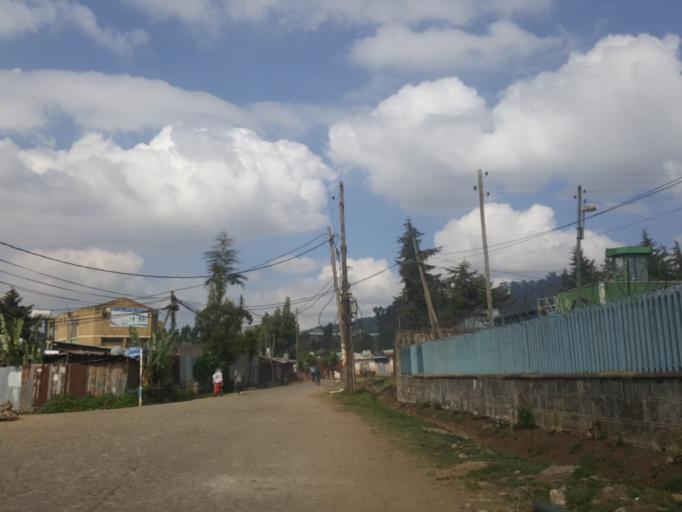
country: ET
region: Adis Abeba
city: Addis Ababa
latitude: 9.0625
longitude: 38.7194
